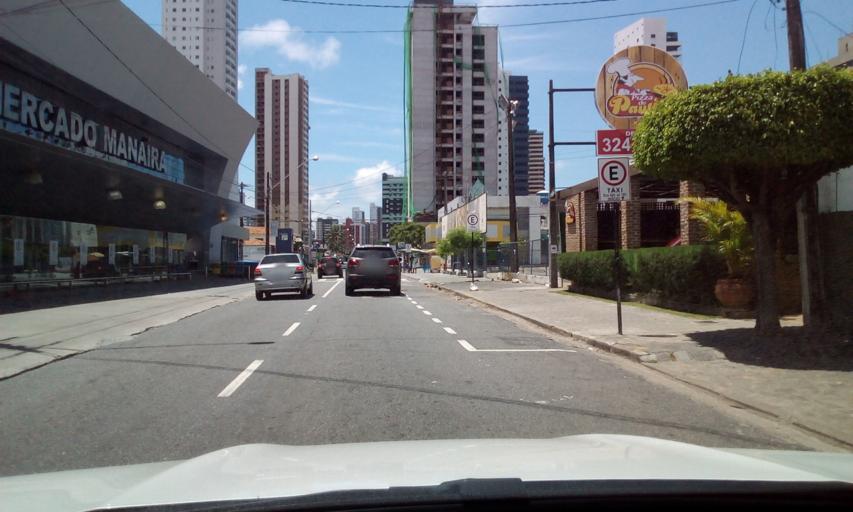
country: BR
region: Paraiba
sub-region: Joao Pessoa
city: Joao Pessoa
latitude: -7.1100
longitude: -34.8317
